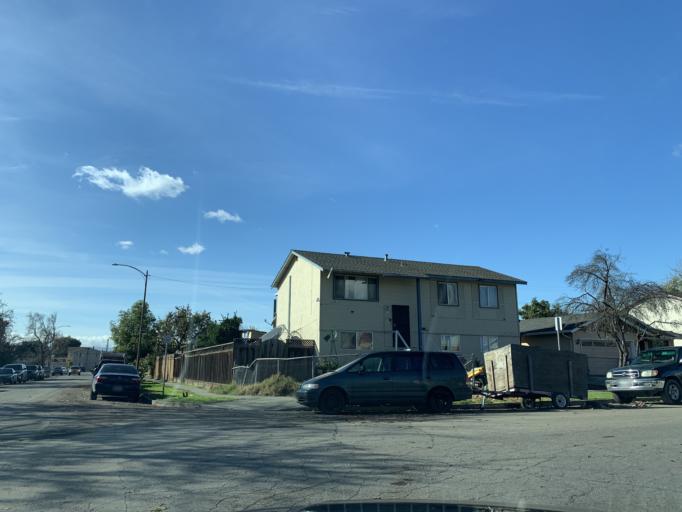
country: US
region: California
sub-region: Santa Clara County
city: Alum Rock
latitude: 37.3427
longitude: -121.8343
